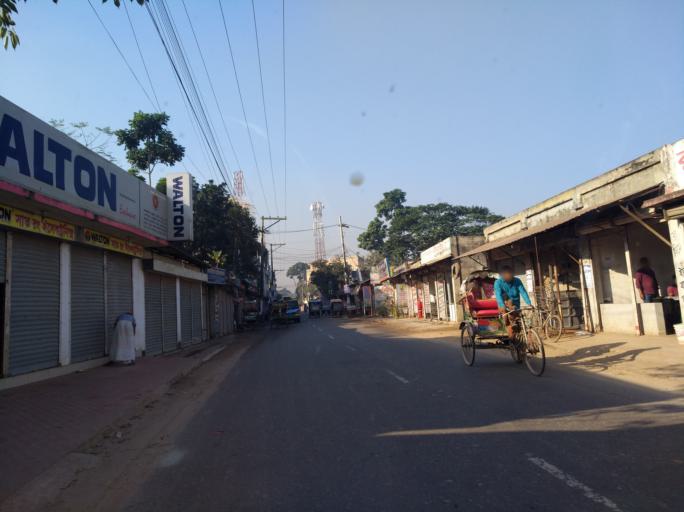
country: BD
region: Dhaka
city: Tungi
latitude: 23.9062
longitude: 90.2853
